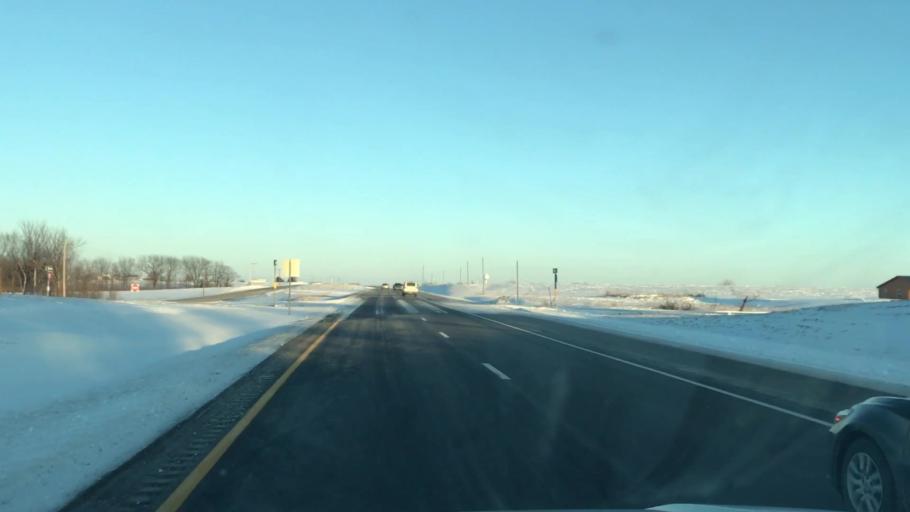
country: US
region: Missouri
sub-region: Clinton County
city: Gower
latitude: 39.7620
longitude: -94.5272
